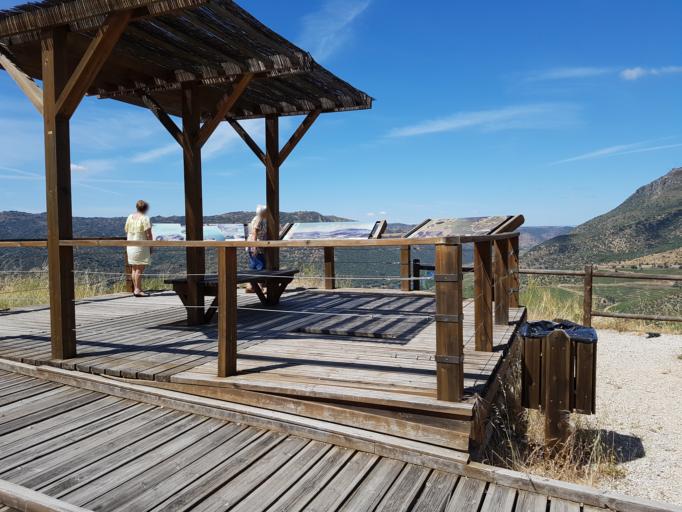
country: ES
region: Castille and Leon
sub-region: Provincia de Salamanca
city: Saucelle
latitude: 41.0425
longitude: -6.7978
